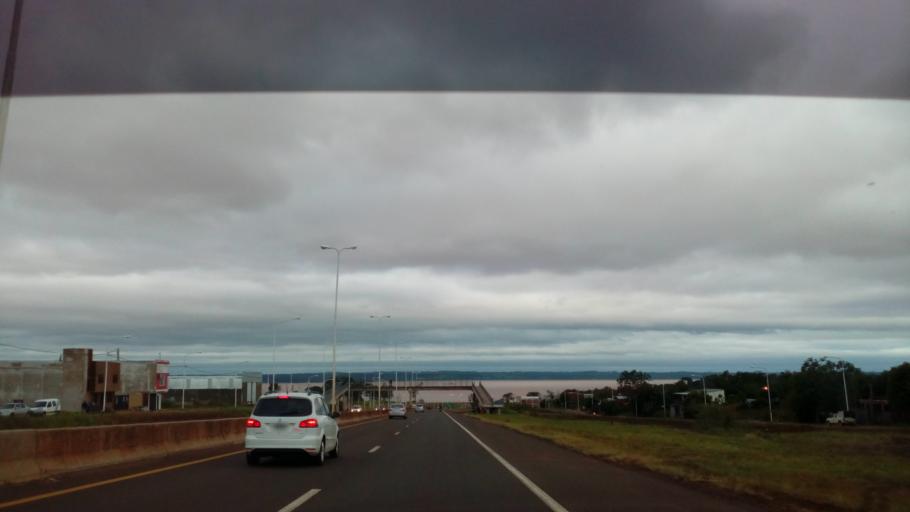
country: AR
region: Misiones
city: Garupa
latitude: -27.4499
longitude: -55.8547
